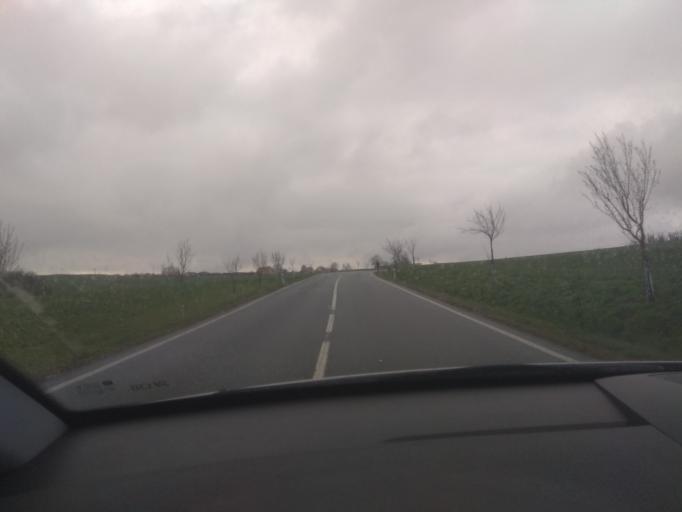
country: CZ
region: South Moravian
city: Zastavka
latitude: 49.1798
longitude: 16.3601
